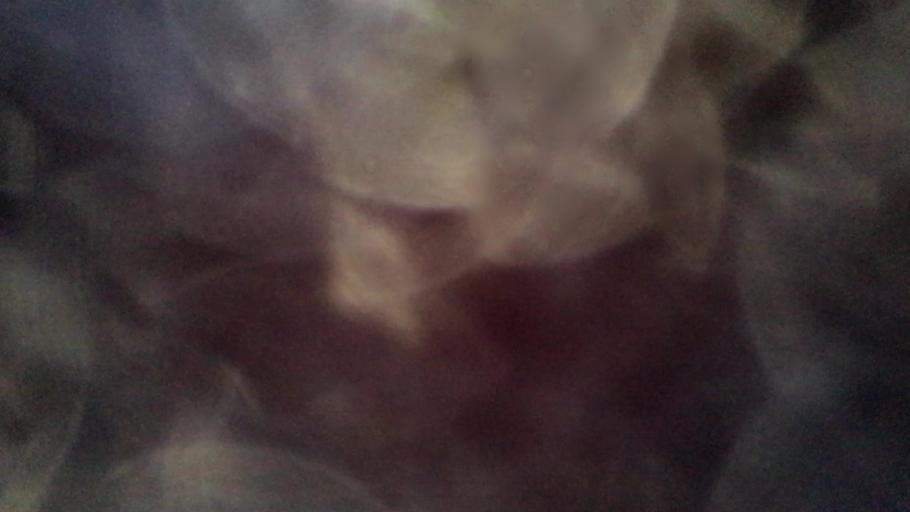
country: US
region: New Jersey
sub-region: Hudson County
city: Guttenberg
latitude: 40.7767
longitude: -74.0027
